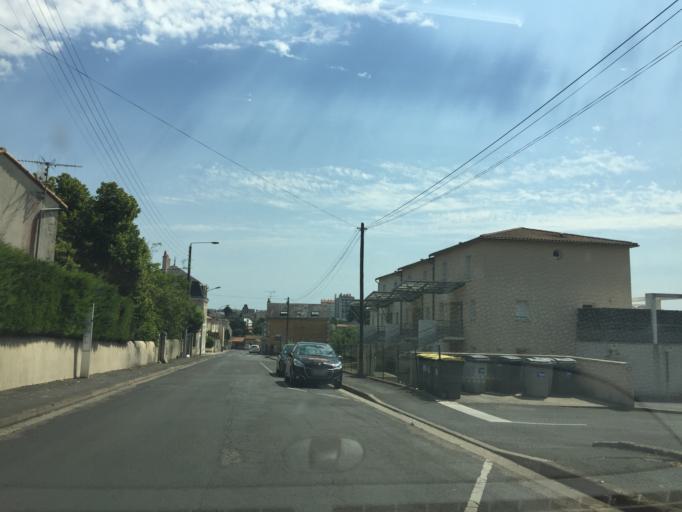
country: FR
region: Poitou-Charentes
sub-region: Departement de la Vienne
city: Poitiers
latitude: 46.5777
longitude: 0.3221
